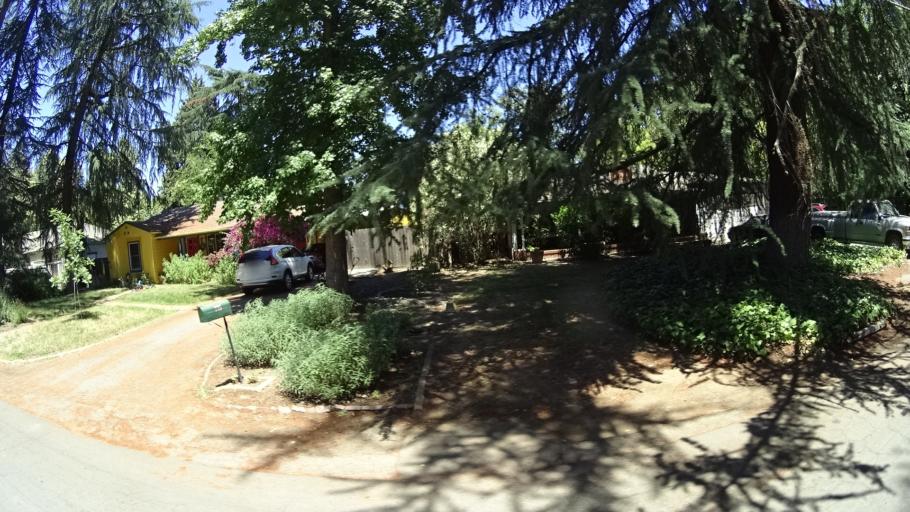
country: US
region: California
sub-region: Fresno County
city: Fresno
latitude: 36.7840
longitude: -119.8015
